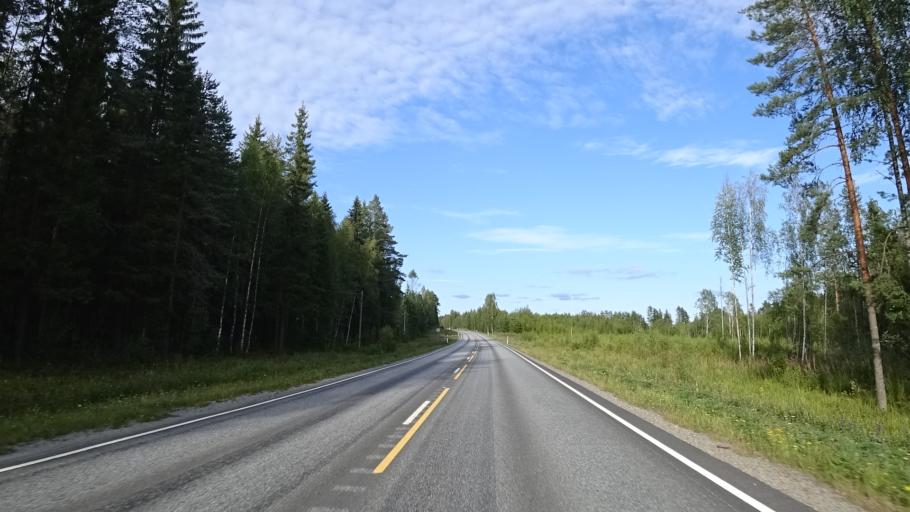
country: FI
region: North Karelia
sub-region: Joensuu
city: Eno
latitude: 62.8113
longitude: 30.1688
